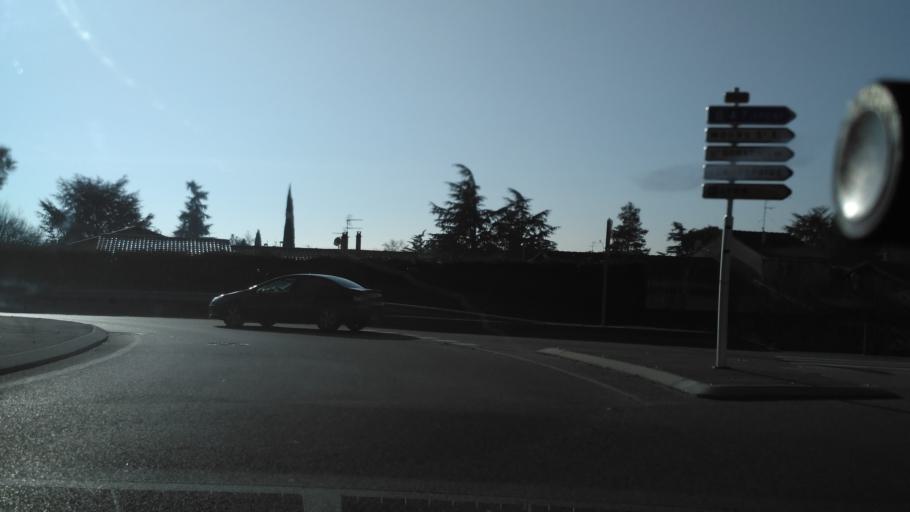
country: FR
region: Rhone-Alpes
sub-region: Departement de la Drome
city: Mours-Saint-Eusebe
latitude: 45.0576
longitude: 5.0644
